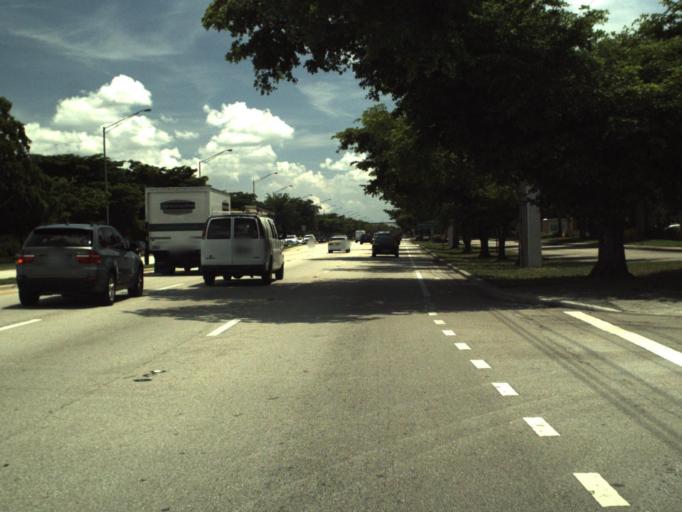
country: US
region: Florida
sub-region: Broward County
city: Plantation
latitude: 26.1467
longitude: -80.2572
